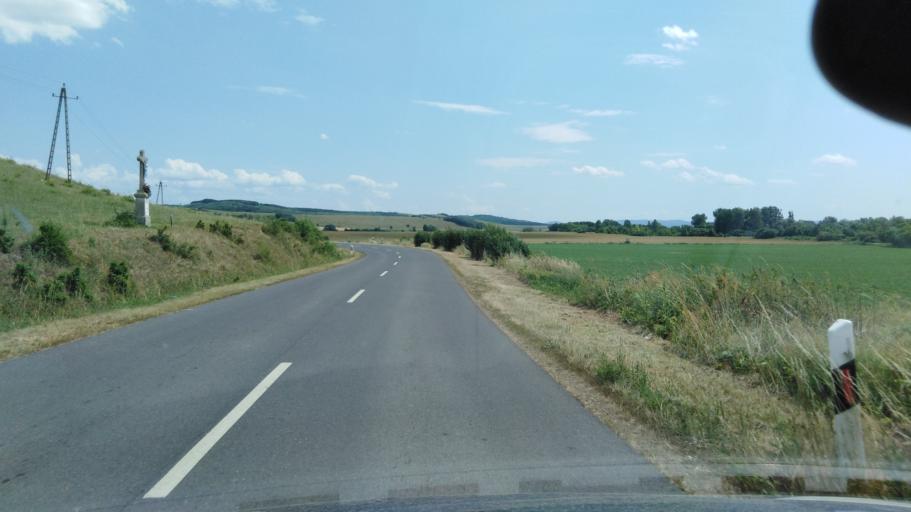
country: HU
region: Nograd
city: Szecseny
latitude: 48.1746
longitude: 19.5272
